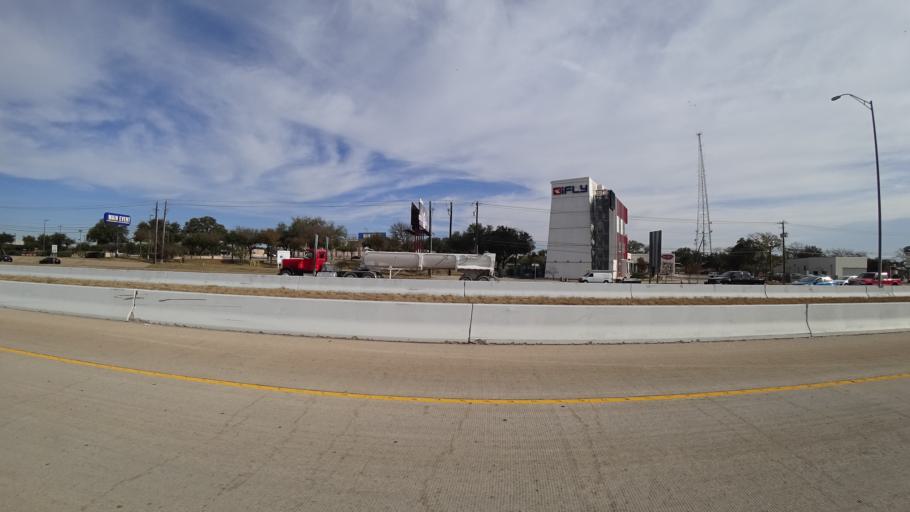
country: US
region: Texas
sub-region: Williamson County
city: Jollyville
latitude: 30.4434
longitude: -97.7858
